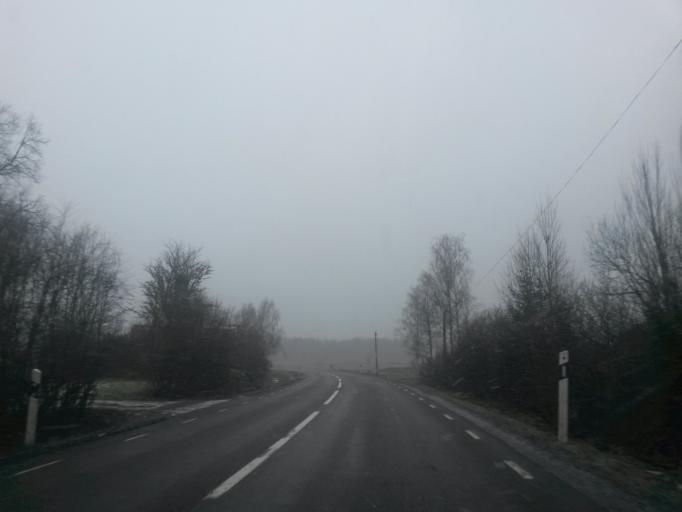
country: SE
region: Vaestra Goetaland
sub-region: Vanersborgs Kommun
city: Vargon
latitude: 58.2272
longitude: 12.4245
